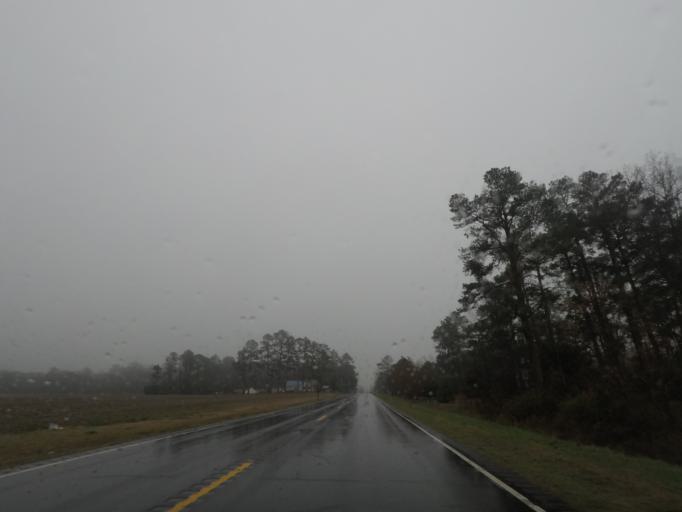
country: US
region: North Carolina
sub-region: Scotland County
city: Laurinburg
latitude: 34.8551
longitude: -79.4574
